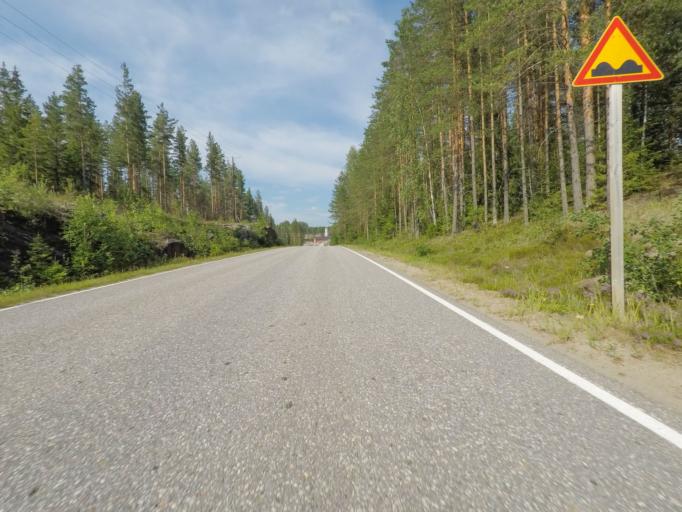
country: FI
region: Southern Savonia
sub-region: Savonlinna
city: Sulkava
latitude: 61.7839
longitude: 28.2410
